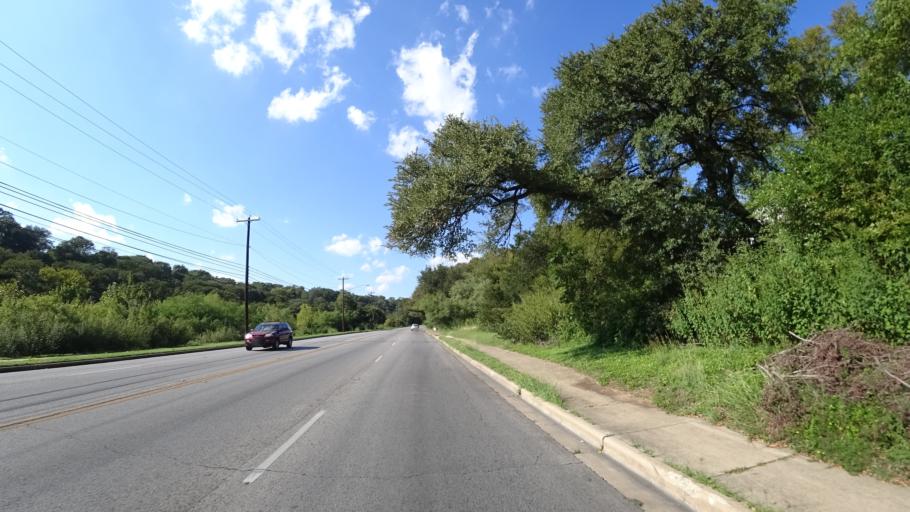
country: US
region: Texas
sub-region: Travis County
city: Austin
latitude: 30.2948
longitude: -97.7479
